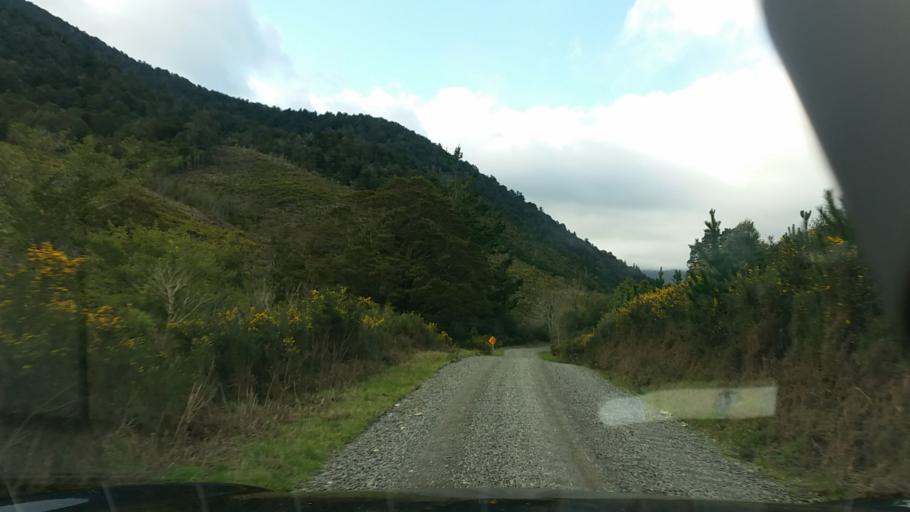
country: NZ
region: Nelson
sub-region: Nelson City
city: Nelson
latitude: -41.1872
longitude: 173.6342
